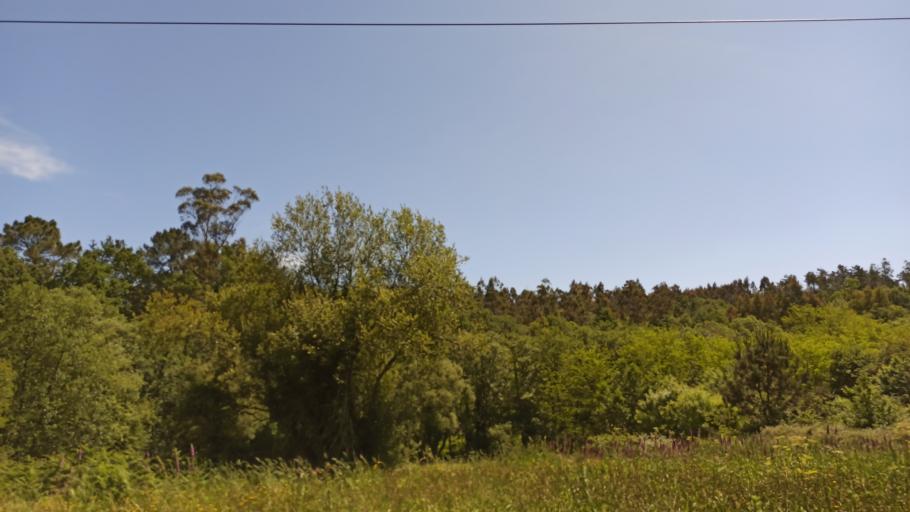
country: ES
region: Galicia
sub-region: Provincia da Coruna
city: Negreira
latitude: 42.9154
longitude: -8.7300
